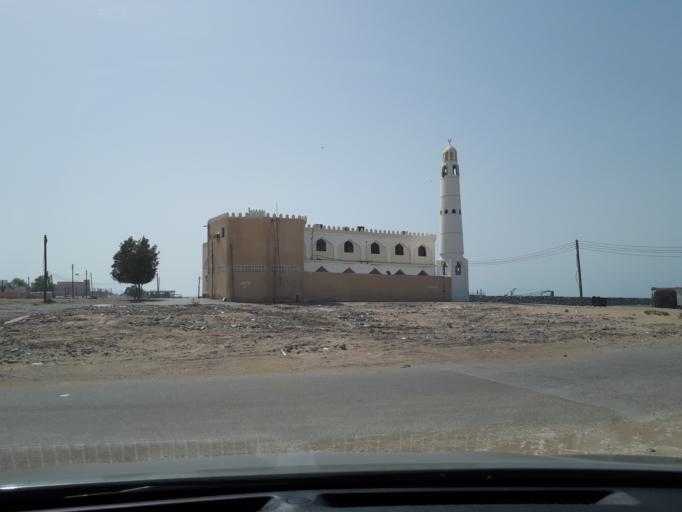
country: OM
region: Al Batinah
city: Barka'
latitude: 23.7087
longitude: 57.9012
